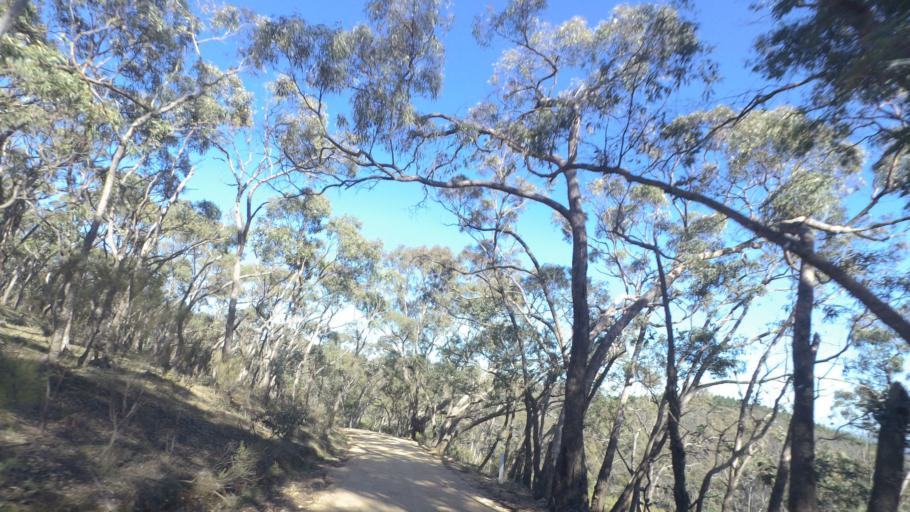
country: AU
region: Victoria
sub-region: Mount Alexander
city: Castlemaine
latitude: -37.0316
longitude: 144.2716
